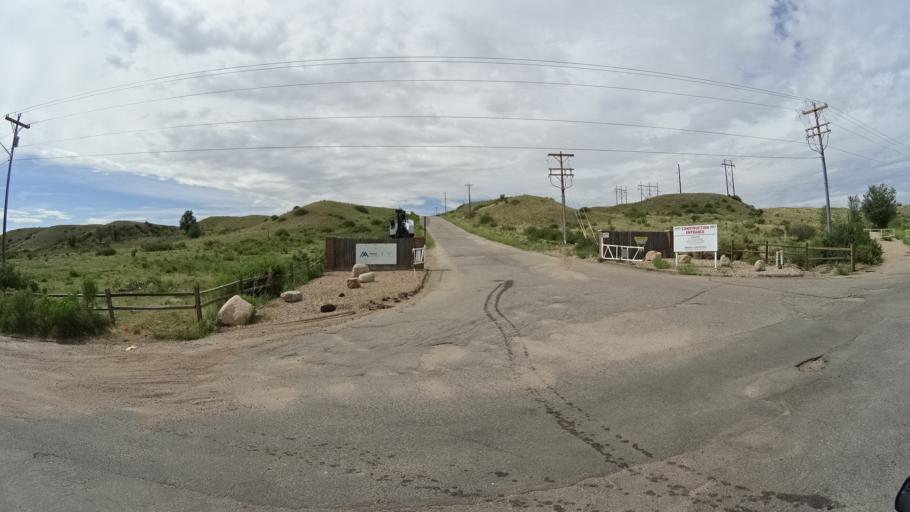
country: US
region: Colorado
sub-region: El Paso County
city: Fountain
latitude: 38.6681
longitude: -104.7186
